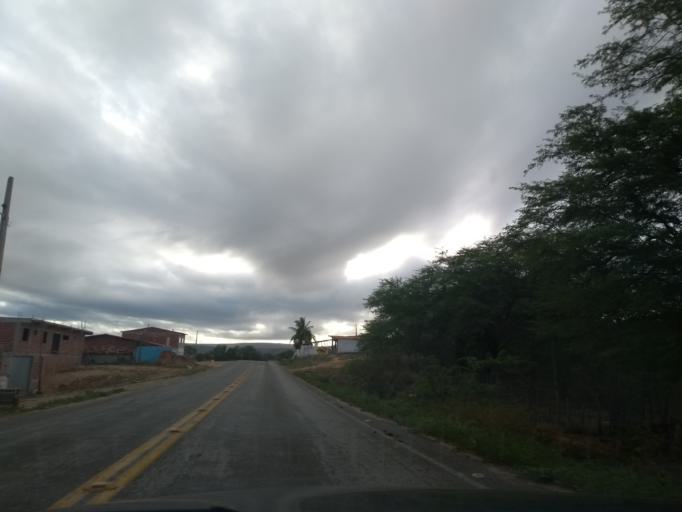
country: BR
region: Bahia
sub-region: Ituacu
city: Ituacu
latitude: -13.7649
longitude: -41.0381
